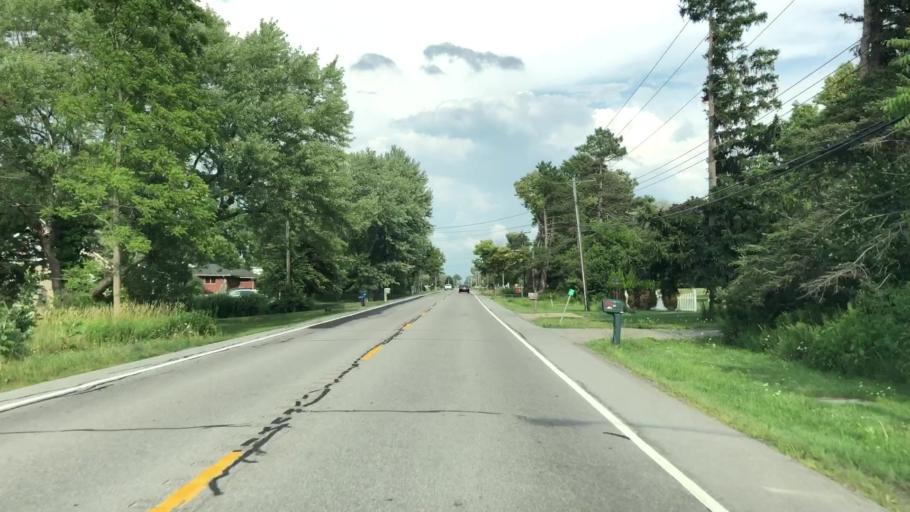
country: US
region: New York
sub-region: Erie County
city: Elma Center
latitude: 42.8555
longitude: -78.6531
